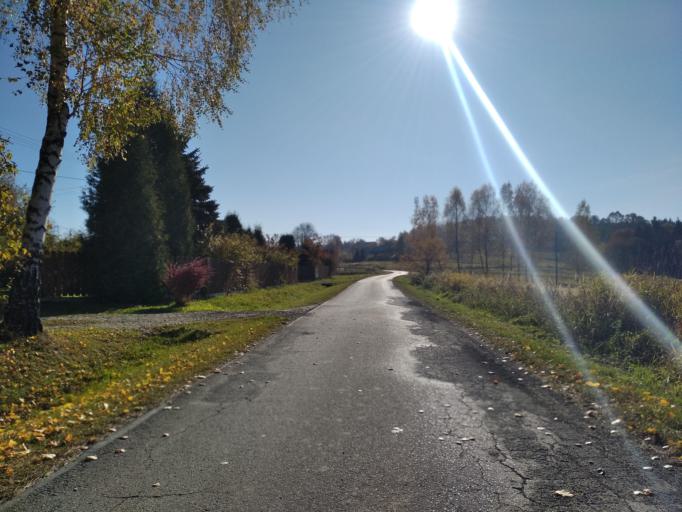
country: PL
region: Subcarpathian Voivodeship
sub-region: Powiat strzyzowski
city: Frysztak
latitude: 49.8529
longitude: 21.5917
